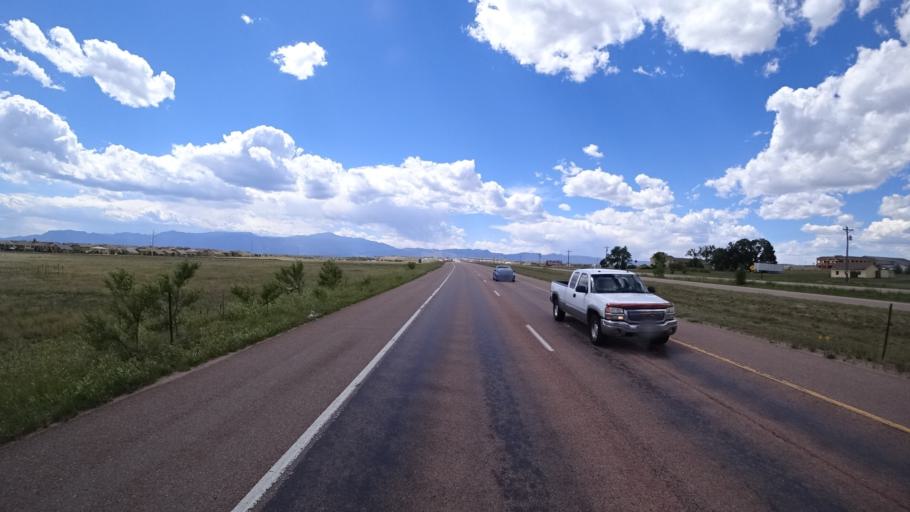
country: US
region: Colorado
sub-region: El Paso County
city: Black Forest
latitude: 38.9406
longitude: -104.6716
